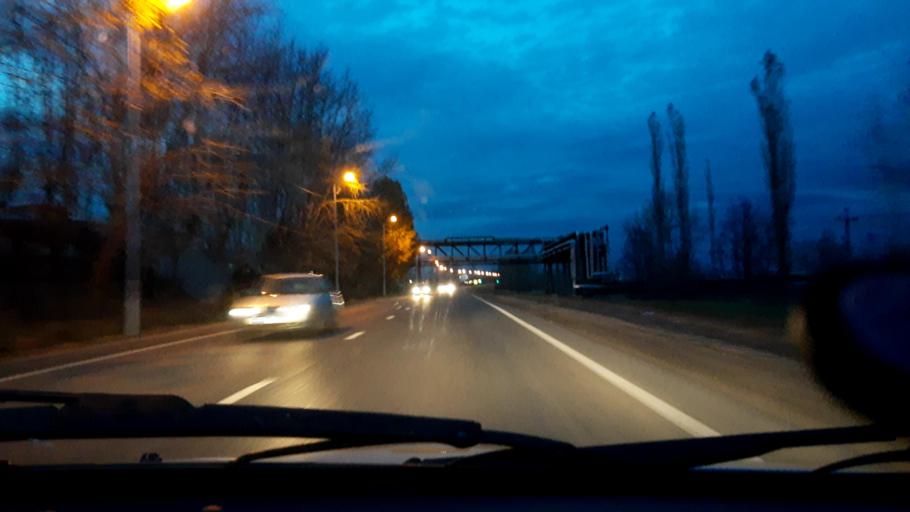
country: RU
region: Bashkortostan
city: Ufa
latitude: 54.8442
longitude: 56.1213
